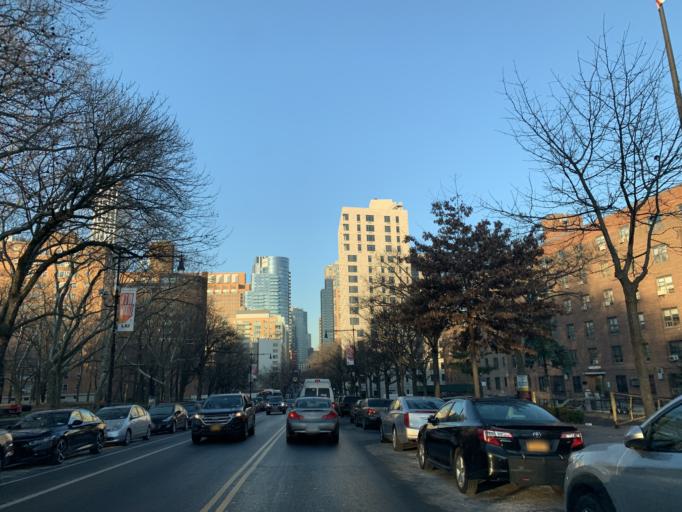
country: US
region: New York
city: New York City
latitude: 40.6934
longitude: -73.9760
